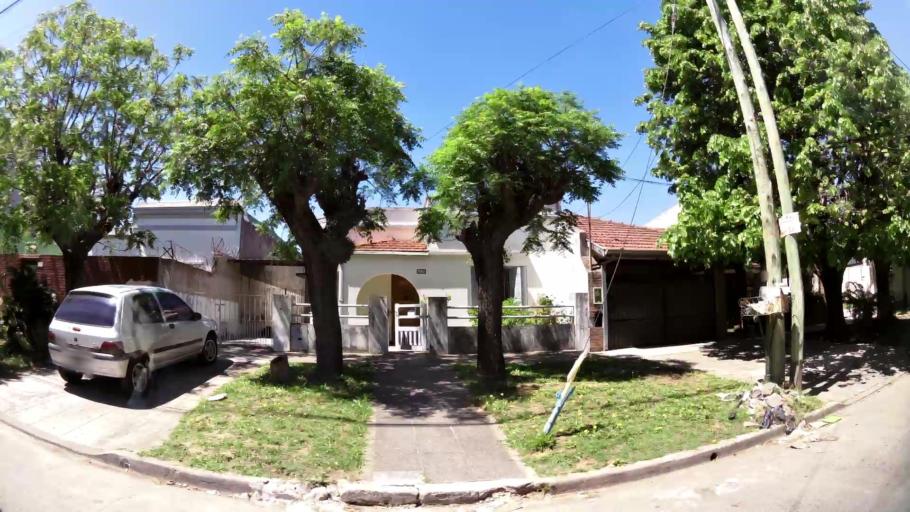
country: AR
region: Buenos Aires
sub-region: Partido de Quilmes
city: Quilmes
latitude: -34.7256
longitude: -58.2697
